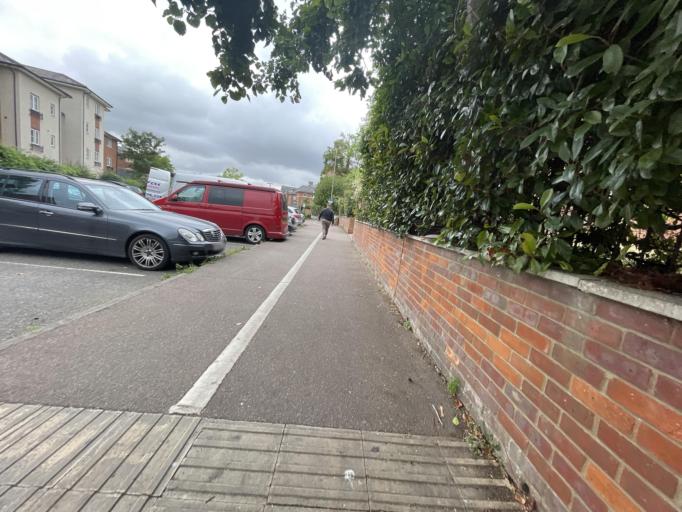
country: GB
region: England
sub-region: Oxfordshire
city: Abingdon
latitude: 51.6727
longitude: -1.2768
